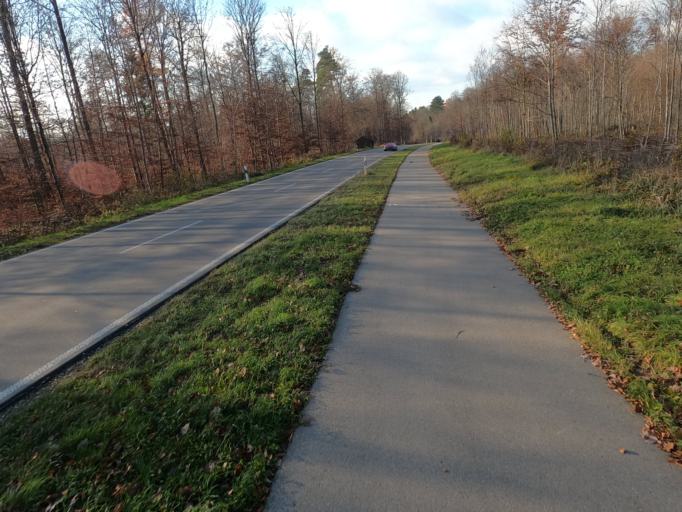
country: DE
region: Baden-Wuerttemberg
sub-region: Regierungsbezirk Stuttgart
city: Schlierbach
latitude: 48.6679
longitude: 9.5418
